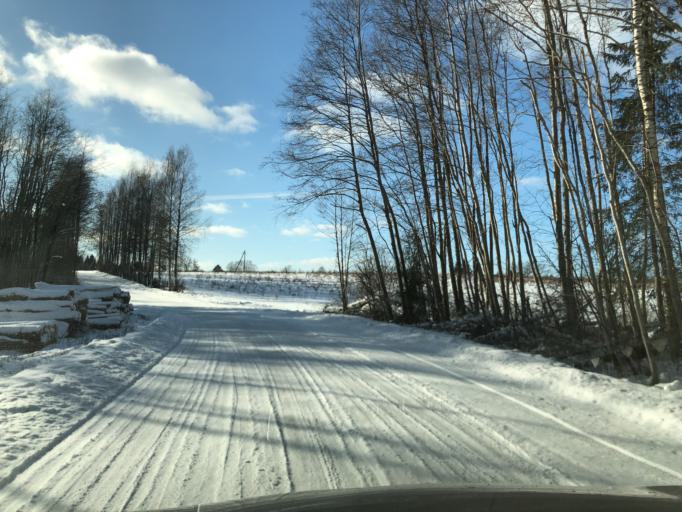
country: EE
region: Jaervamaa
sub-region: Paide linn
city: Paide
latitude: 59.0449
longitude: 25.4760
